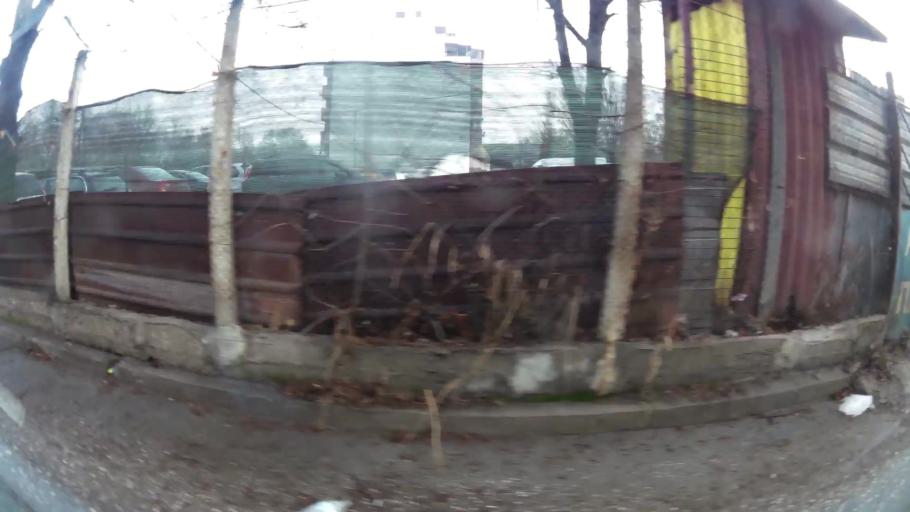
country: BG
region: Sofia-Capital
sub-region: Stolichna Obshtina
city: Sofia
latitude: 42.7311
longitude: 23.3117
